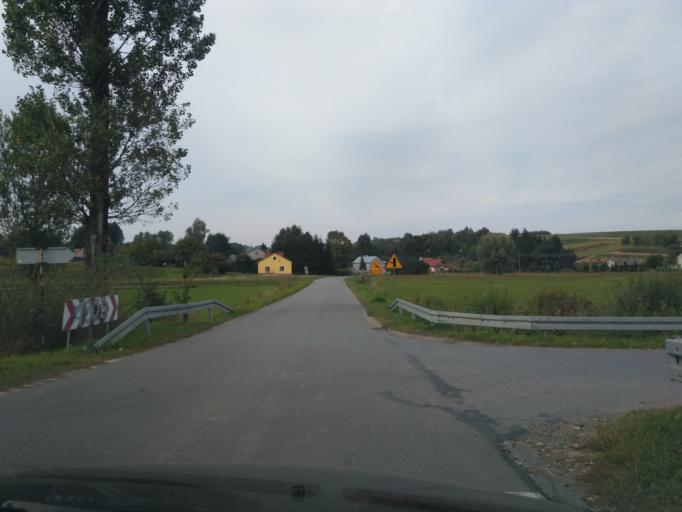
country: PL
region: Subcarpathian Voivodeship
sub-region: Powiat rzeszowski
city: Zglobien
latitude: 50.0318
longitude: 21.8436
